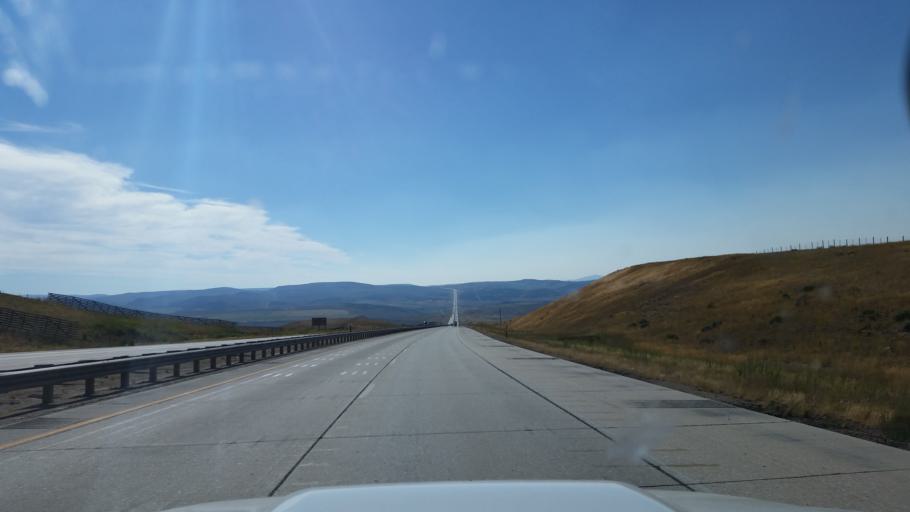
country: US
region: Wyoming
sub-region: Uinta County
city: Mountain View
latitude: 41.2974
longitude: -110.5589
